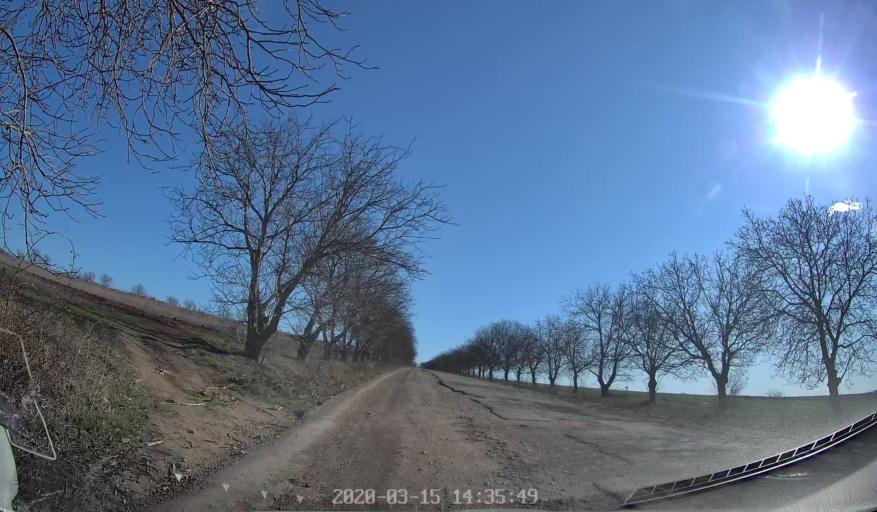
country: MD
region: Orhei
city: Orhei
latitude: 47.3280
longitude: 28.9250
